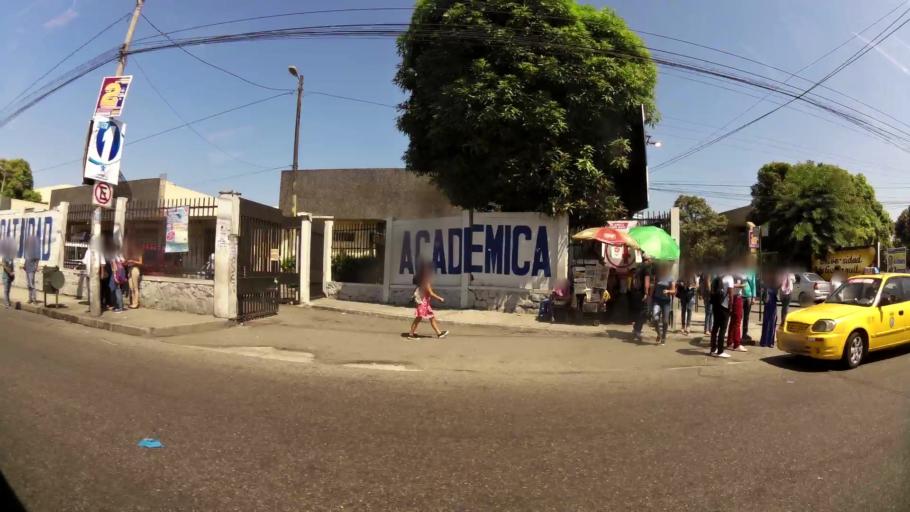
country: EC
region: Guayas
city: Guayaquil
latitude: -2.1820
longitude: -79.8962
